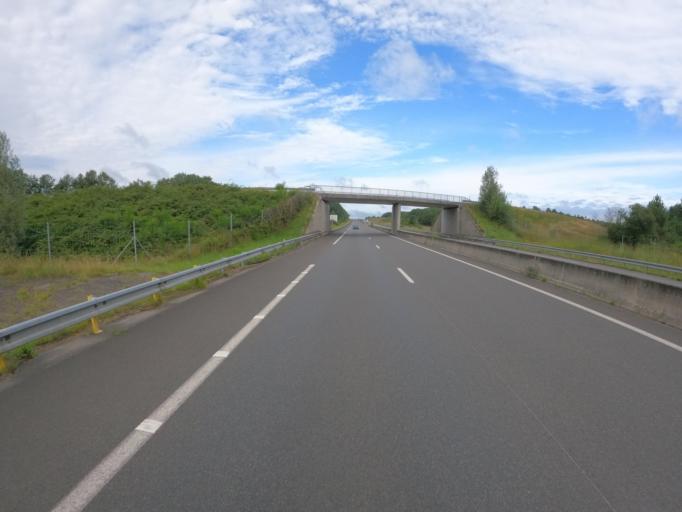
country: FR
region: Centre
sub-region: Departement d'Indre-et-Loire
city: Langeais
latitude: 47.3459
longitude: 0.3953
